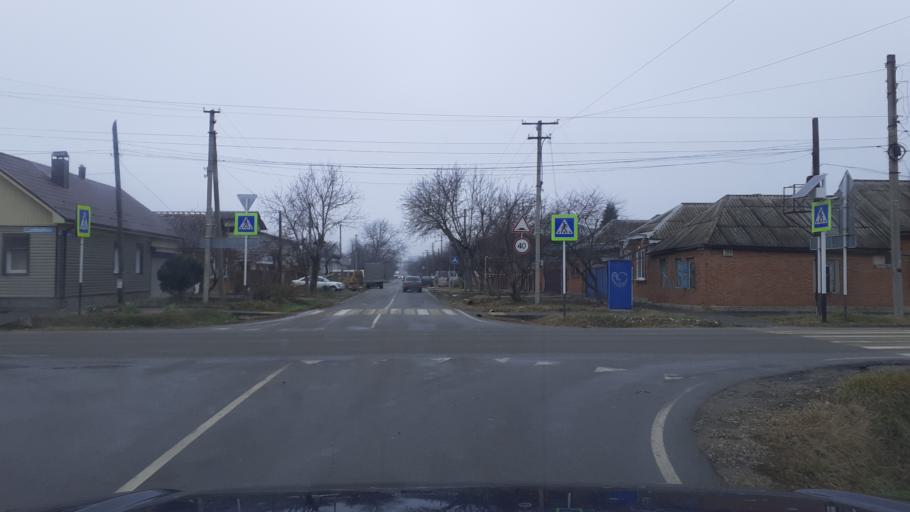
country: RU
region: Adygeya
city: Maykop
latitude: 44.6188
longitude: 40.0790
